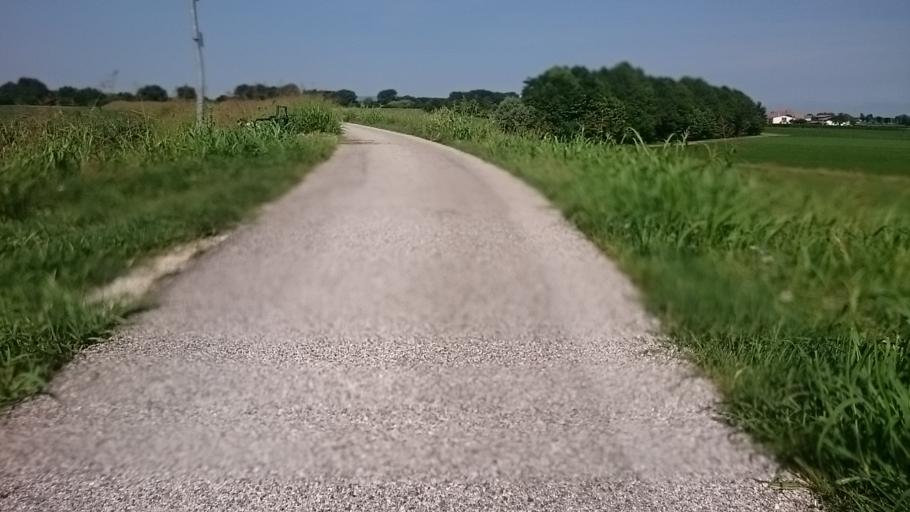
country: IT
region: Veneto
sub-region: Provincia di Padova
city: Saccolongo
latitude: 45.4037
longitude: 11.7631
